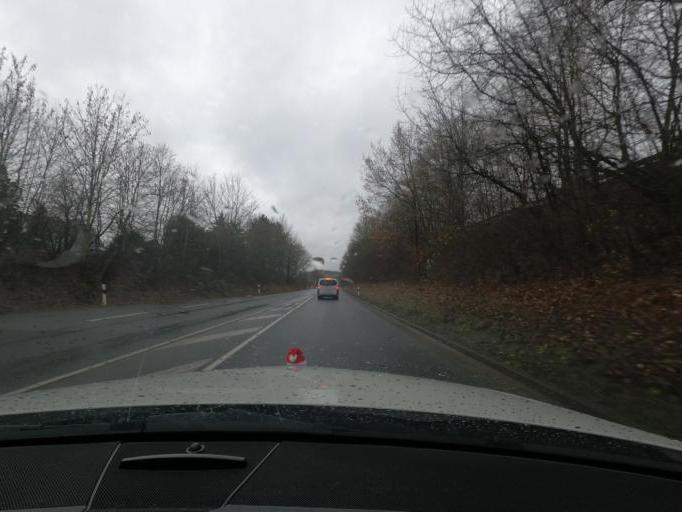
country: DE
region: Lower Saxony
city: Einbeck
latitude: 51.8004
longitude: 9.9230
